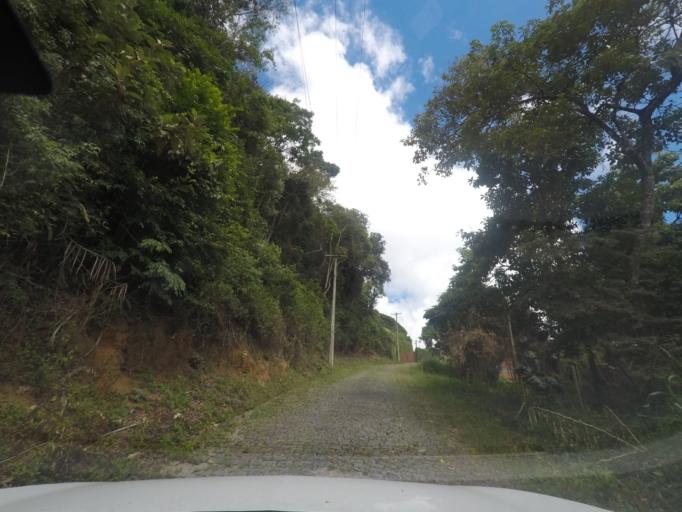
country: BR
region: Rio de Janeiro
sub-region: Teresopolis
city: Teresopolis
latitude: -22.3997
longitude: -42.9861
